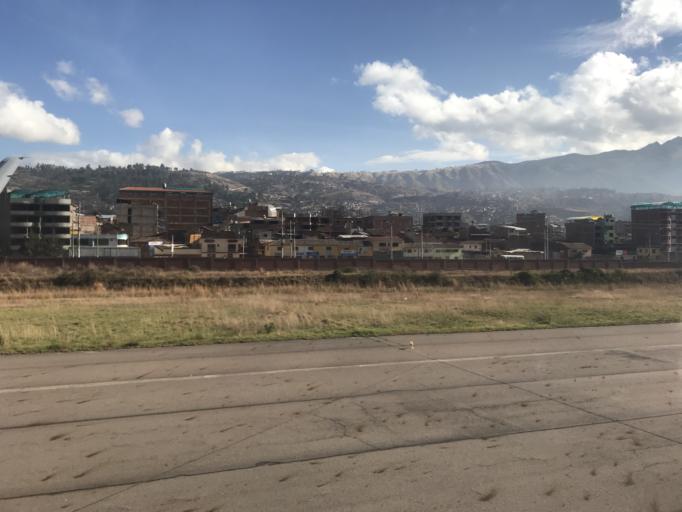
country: PE
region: Cusco
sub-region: Provincia de Cusco
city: Cusco
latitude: -13.5358
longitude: -71.9386
